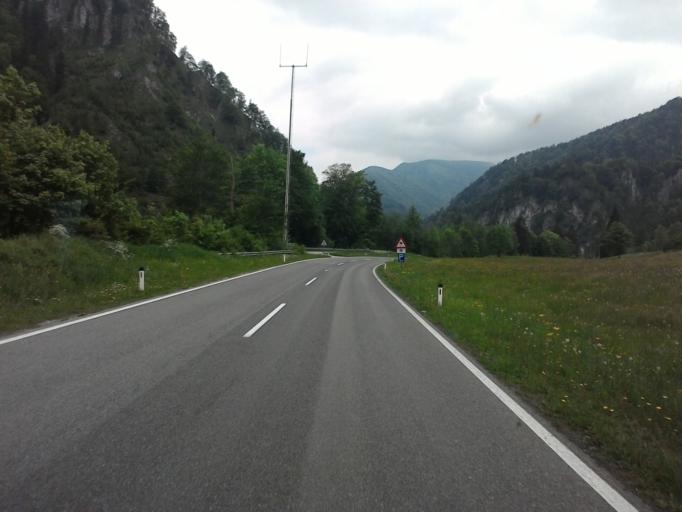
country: AT
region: Styria
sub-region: Politischer Bezirk Liezen
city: Altenmarkt bei Sankt Gallen
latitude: 47.7662
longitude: 14.6485
